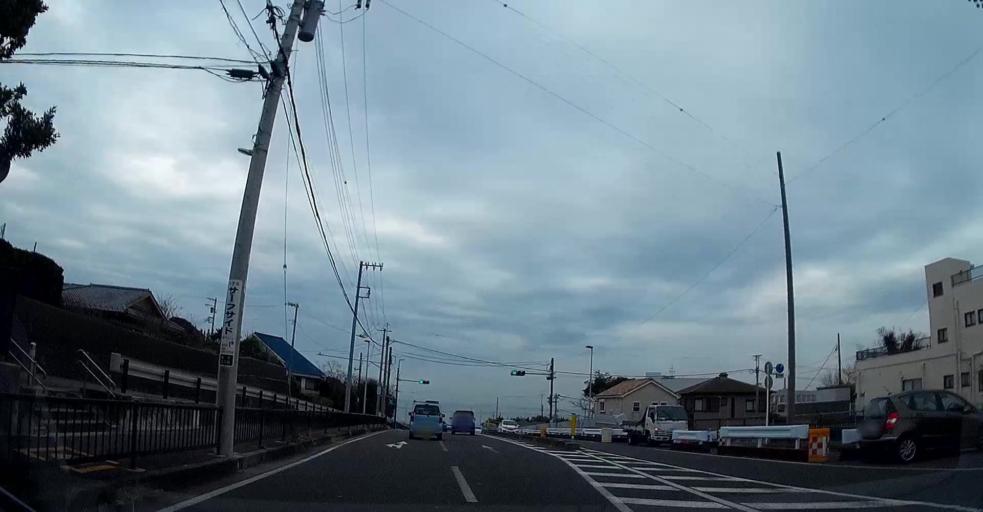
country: JP
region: Kanagawa
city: Yokosuka
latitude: 35.2063
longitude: 139.6789
